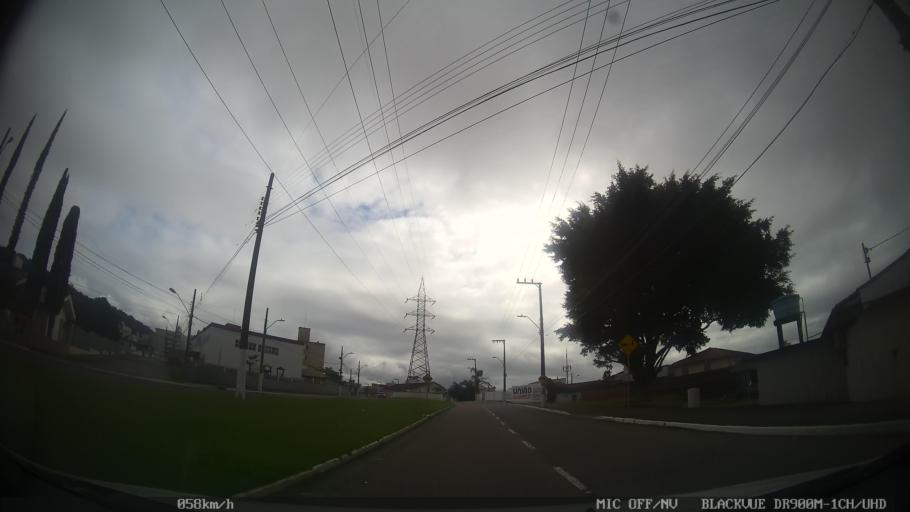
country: BR
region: Santa Catarina
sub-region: Sao Jose
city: Campinas
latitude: -27.5803
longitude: -48.6214
